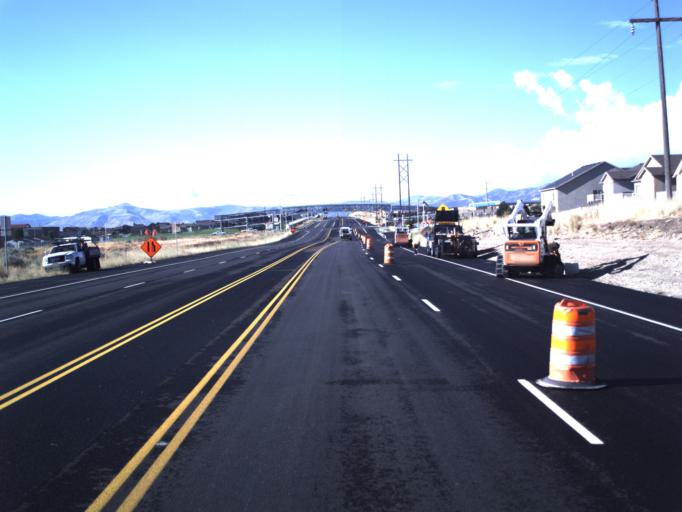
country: US
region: Utah
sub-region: Salt Lake County
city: Oquirrh
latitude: 40.6054
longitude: -112.0563
